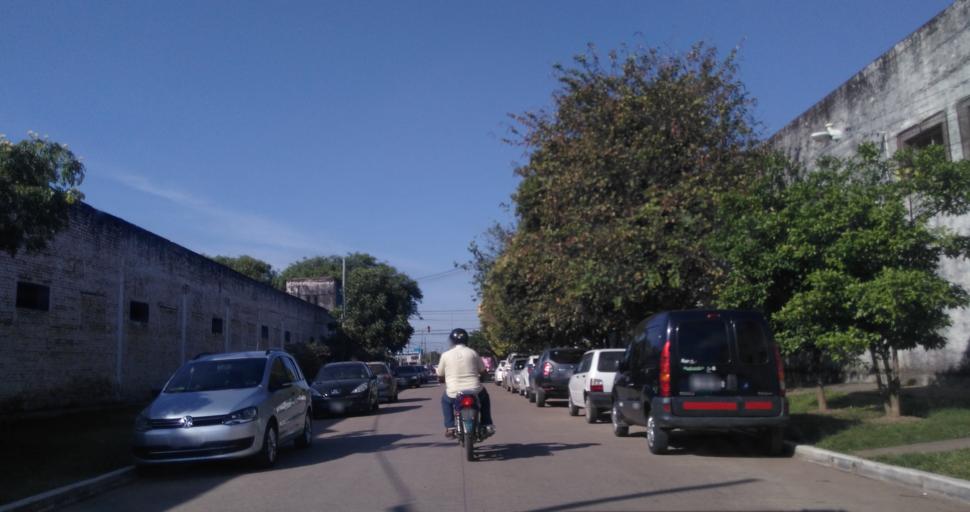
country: AR
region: Chaco
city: Resistencia
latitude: -27.4673
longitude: -58.9669
